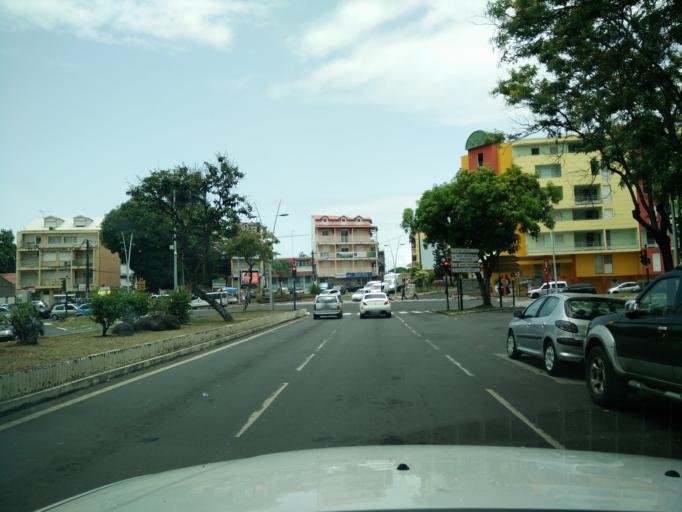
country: GP
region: Guadeloupe
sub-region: Guadeloupe
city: Pointe-a-Pitre
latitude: 16.2404
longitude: -61.5320
